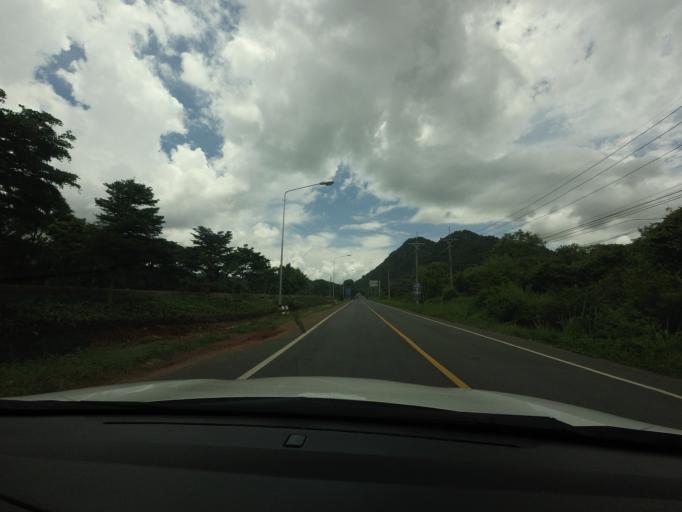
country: TH
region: Sara Buri
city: Muak Lek
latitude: 14.5513
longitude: 101.3234
